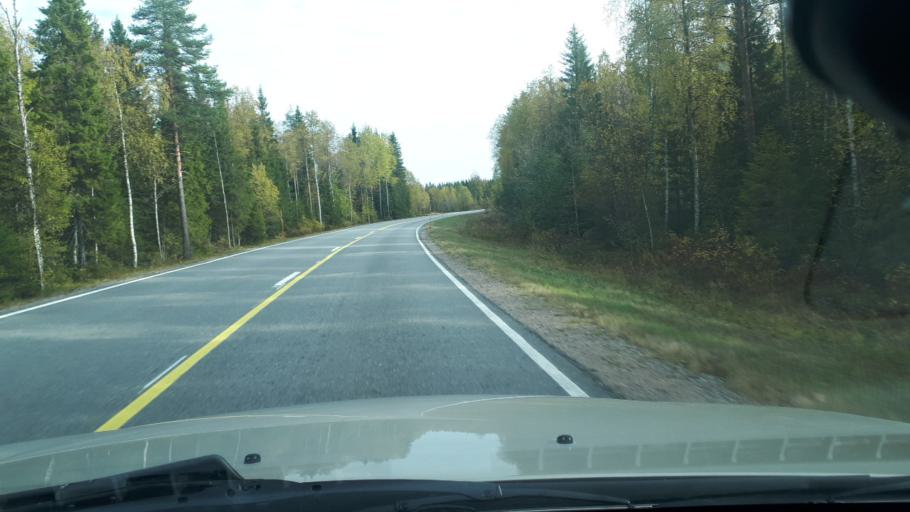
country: FI
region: Lapland
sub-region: Rovaniemi
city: Rovaniemi
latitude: 65.9612
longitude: 25.9478
